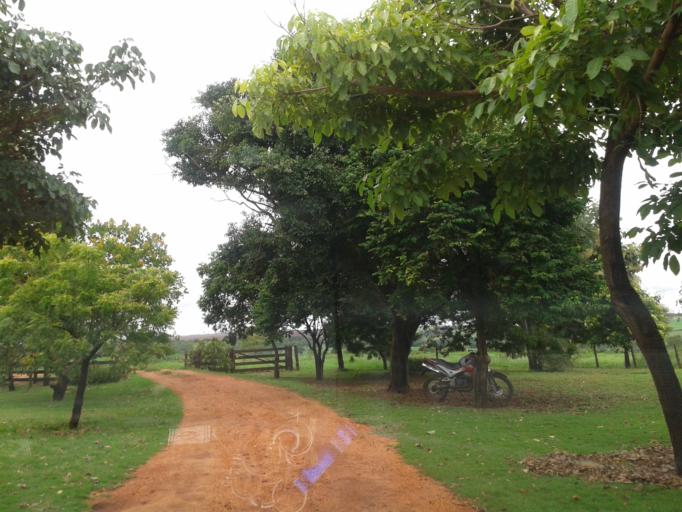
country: BR
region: Minas Gerais
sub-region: Santa Vitoria
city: Santa Vitoria
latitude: -18.7410
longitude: -49.9874
